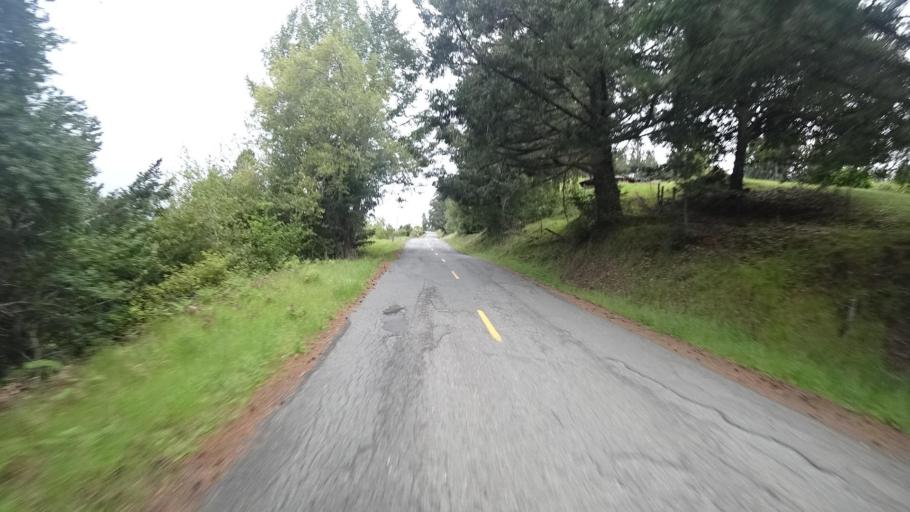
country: US
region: California
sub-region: Humboldt County
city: Redway
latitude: 40.2848
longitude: -123.7991
